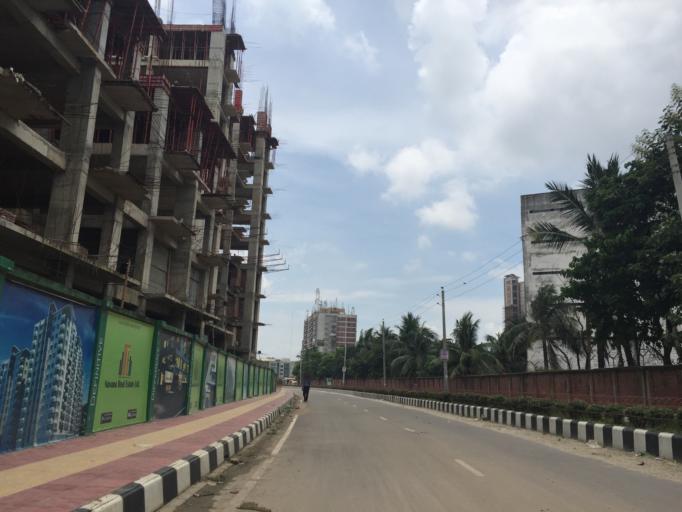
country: BD
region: Dhaka
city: Azimpur
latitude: 23.8041
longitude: 90.3831
